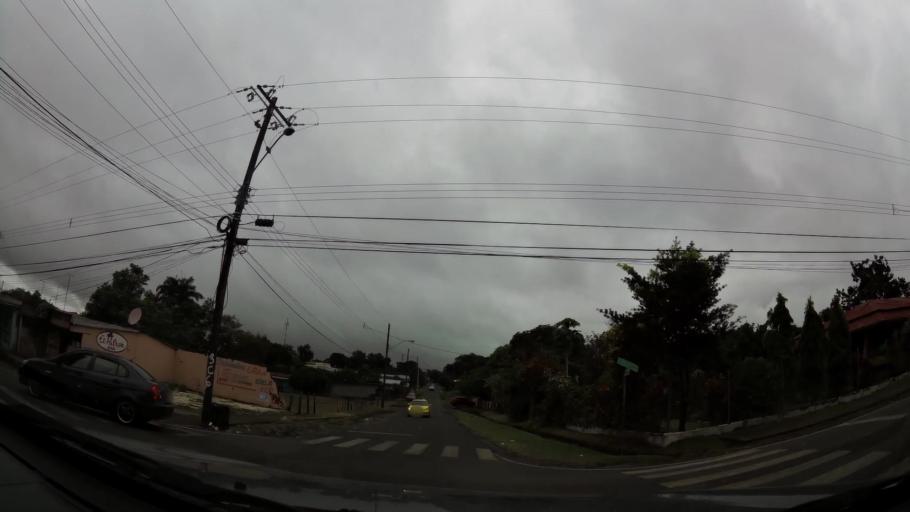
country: PA
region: Chiriqui
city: La Concepcion
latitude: 8.5192
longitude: -82.6196
